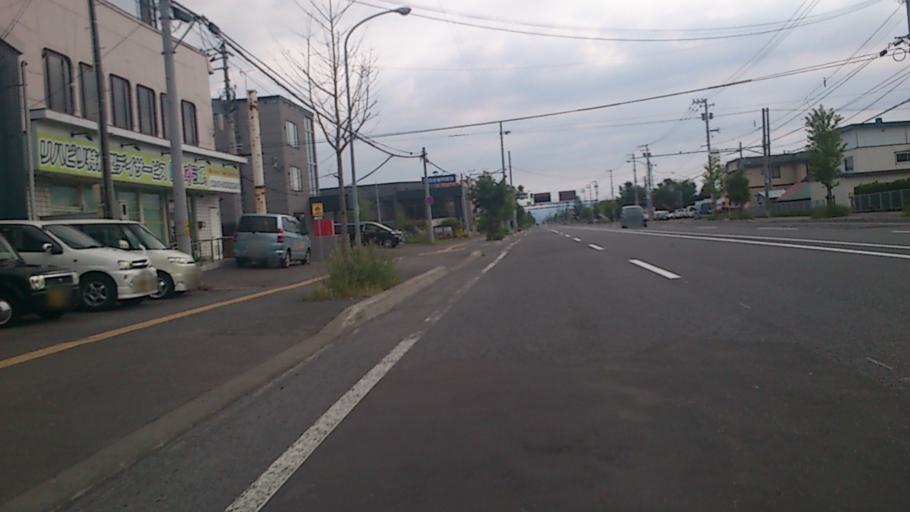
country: JP
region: Hokkaido
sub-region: Asahikawa-shi
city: Asahikawa
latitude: 43.8173
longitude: 142.4446
